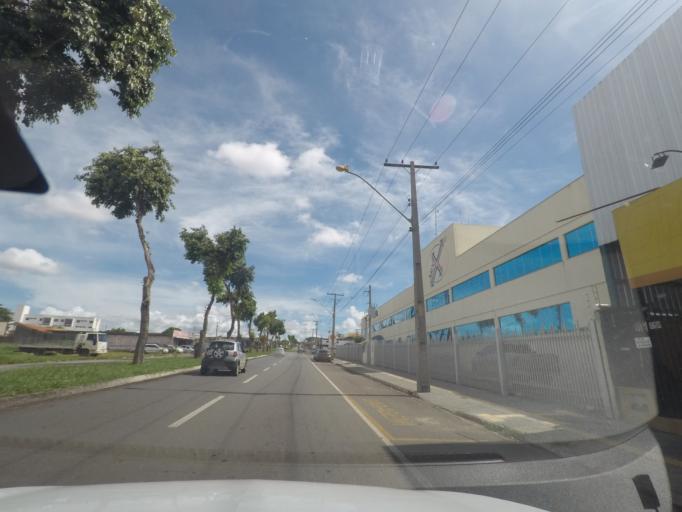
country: BR
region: Goias
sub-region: Goiania
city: Goiania
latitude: -16.7423
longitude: -49.3292
